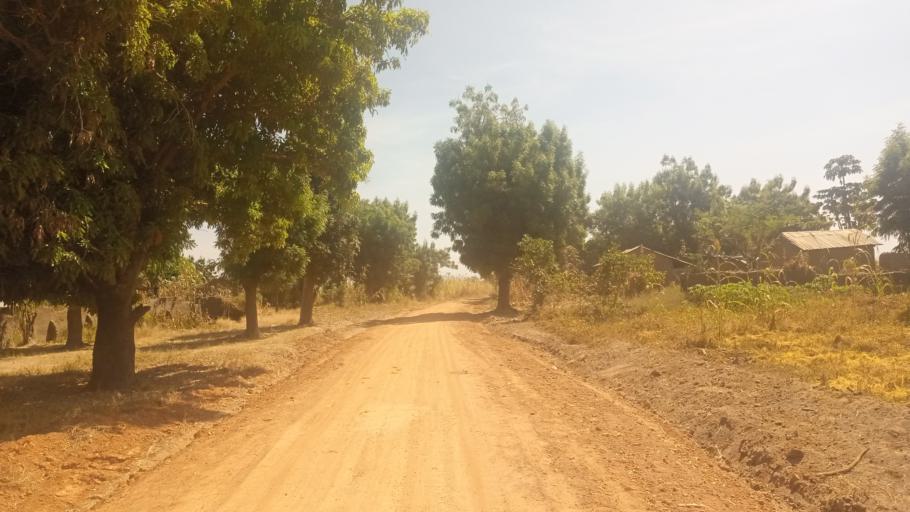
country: NG
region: Adamawa
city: Madagali
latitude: 10.8500
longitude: 13.3918
